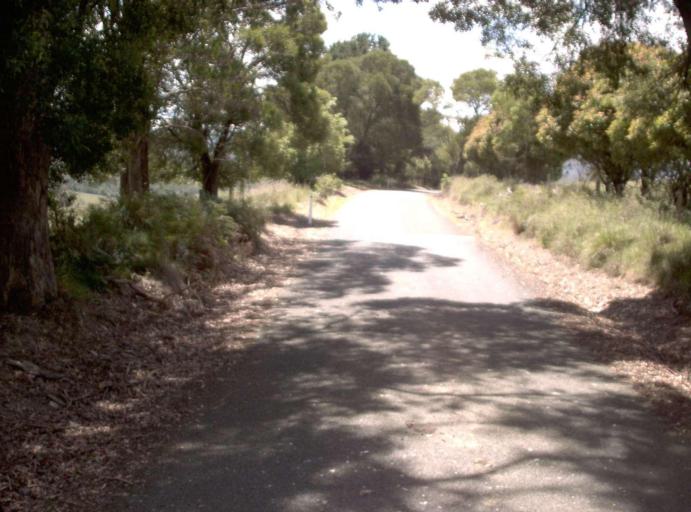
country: AU
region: New South Wales
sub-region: Bombala
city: Bombala
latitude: -37.4218
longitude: 149.0093
